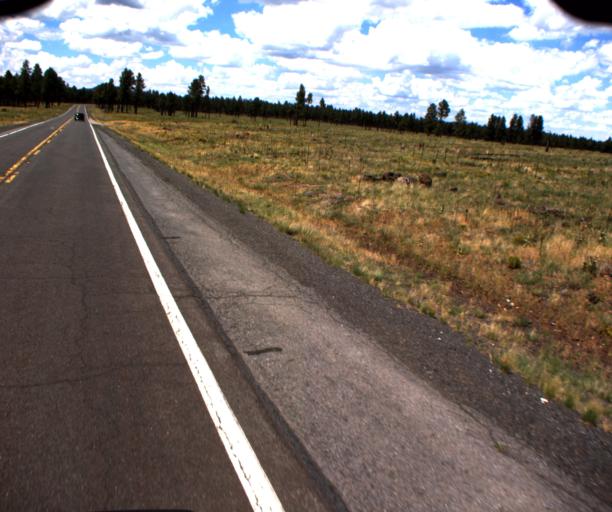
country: US
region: Arizona
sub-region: Coconino County
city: Parks
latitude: 35.4477
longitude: -111.7674
